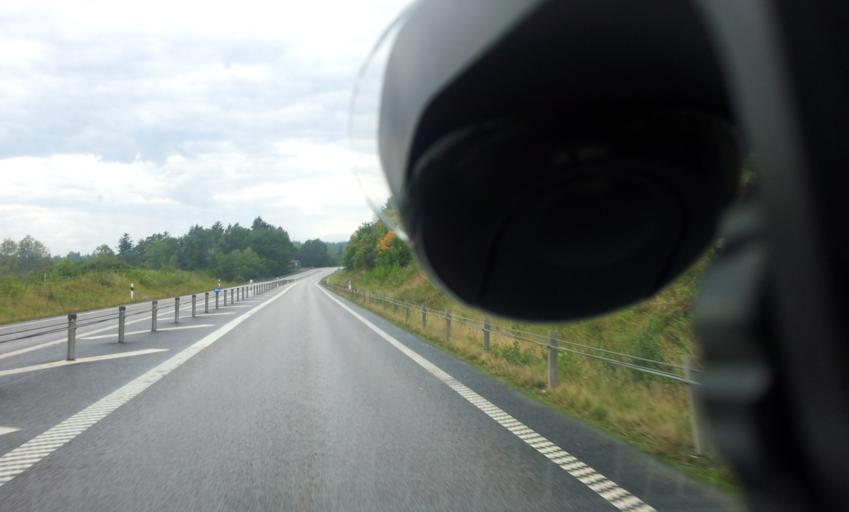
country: SE
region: Kalmar
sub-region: Vasterviks Kommun
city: Gamleby
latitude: 57.9343
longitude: 16.4111
